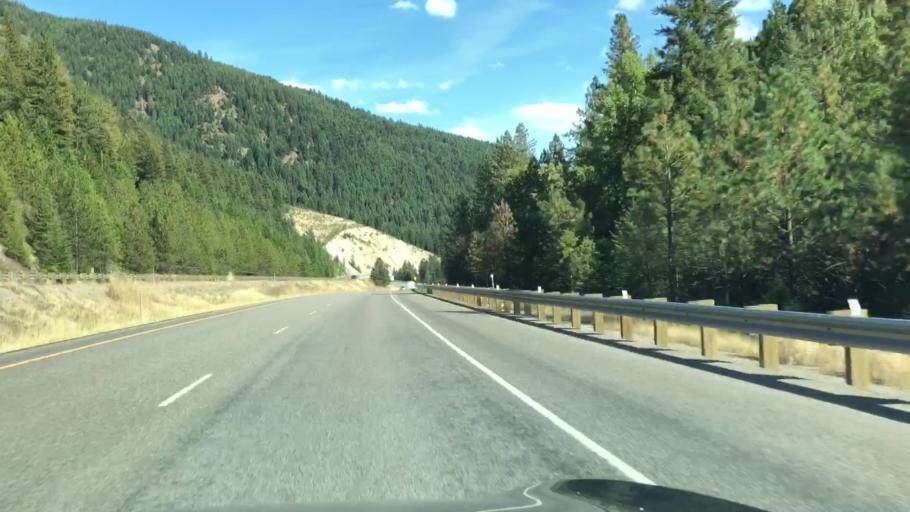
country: US
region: Montana
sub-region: Sanders County
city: Thompson Falls
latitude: 47.3135
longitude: -115.2216
